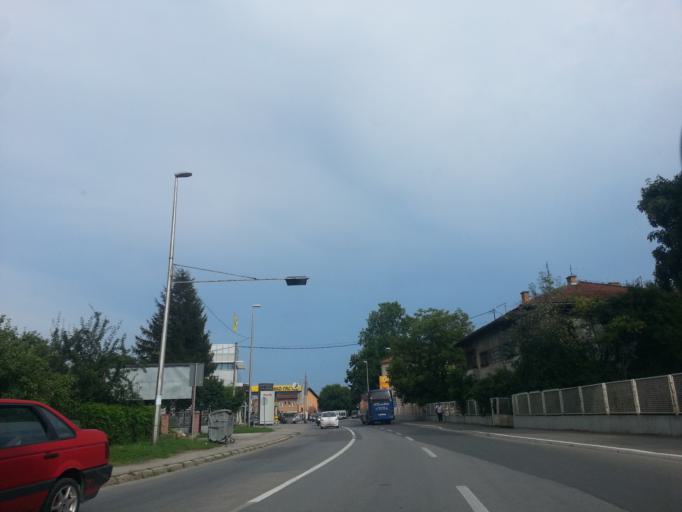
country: BA
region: Brcko
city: Brcko
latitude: 44.8778
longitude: 18.7960
